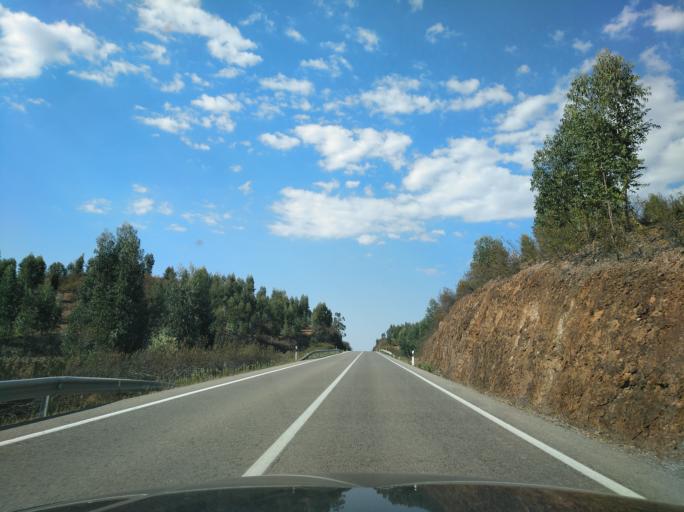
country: ES
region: Andalusia
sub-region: Provincia de Huelva
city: Santa Barbara de Casa
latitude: 37.8186
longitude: -7.2097
